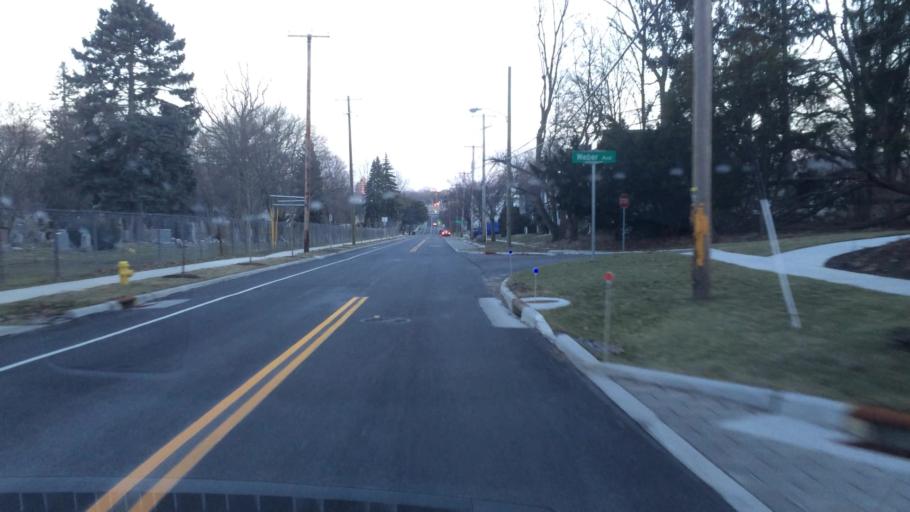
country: US
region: Ohio
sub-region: Summit County
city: Akron
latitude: 41.0959
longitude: -81.5328
